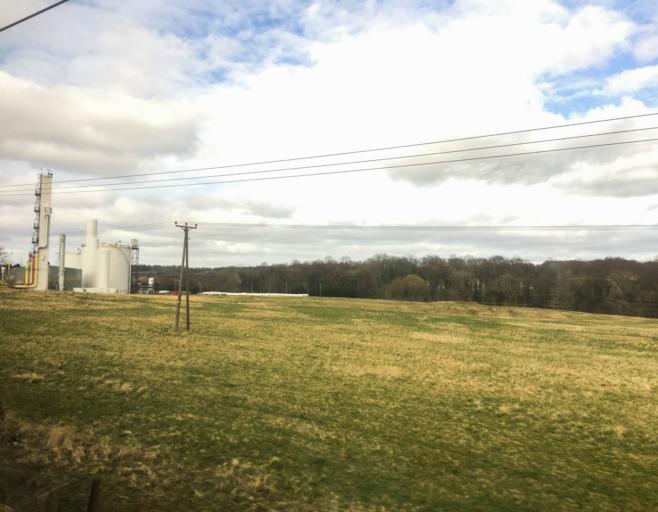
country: GB
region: Scotland
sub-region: North Lanarkshire
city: Newarthill
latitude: 55.7988
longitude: -3.9529
